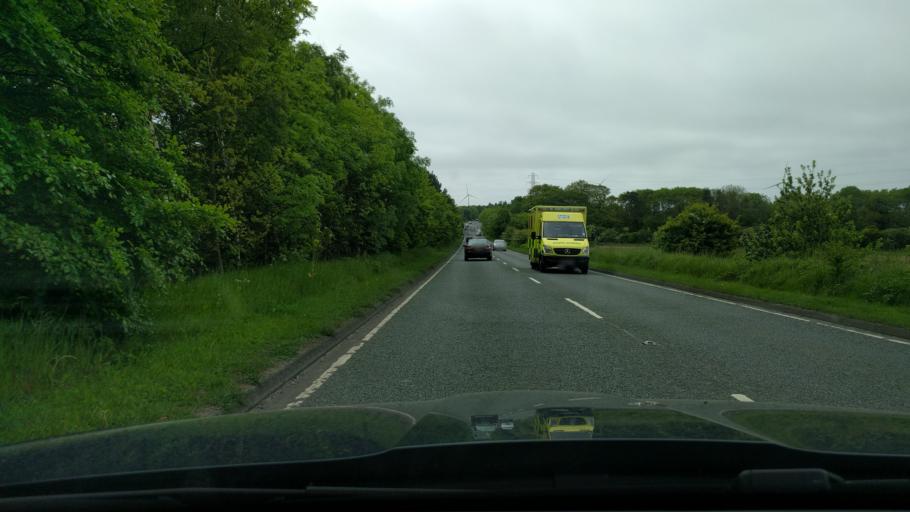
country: GB
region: England
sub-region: Northumberland
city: Cresswell
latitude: 55.2200
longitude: -1.5723
